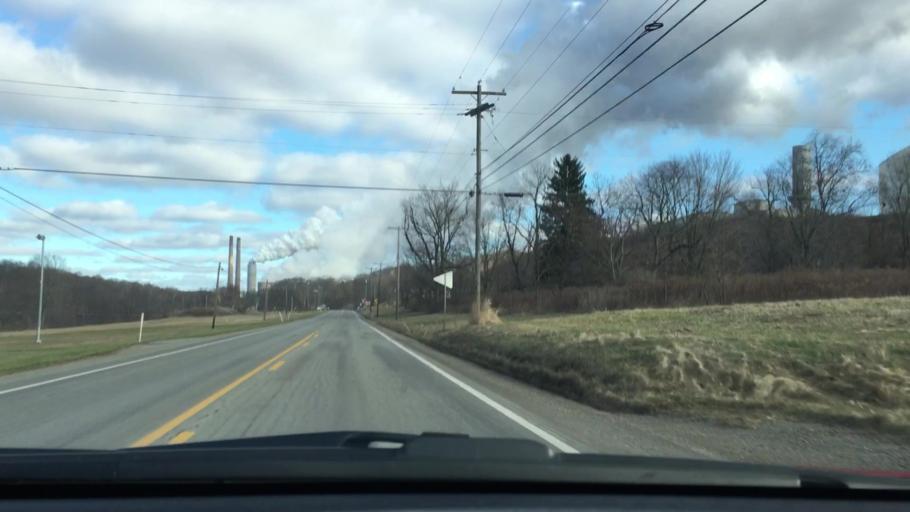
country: US
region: Pennsylvania
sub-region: Westmoreland County
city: Avonmore
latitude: 40.6365
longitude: -79.3555
